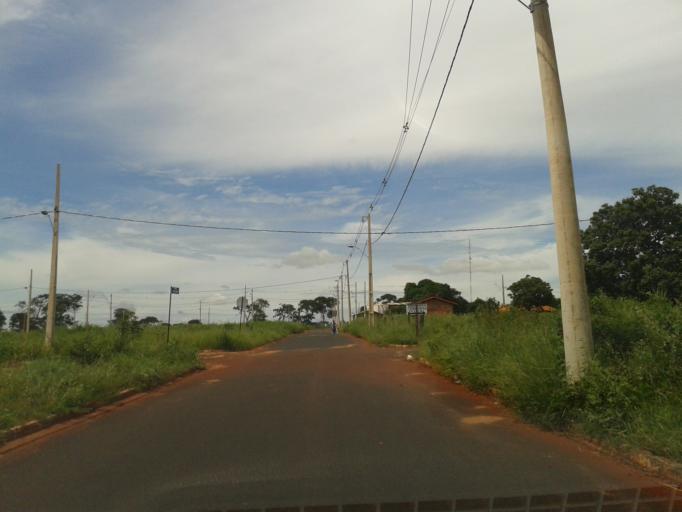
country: BR
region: Minas Gerais
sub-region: Santa Vitoria
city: Santa Vitoria
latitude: -18.8341
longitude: -50.1408
